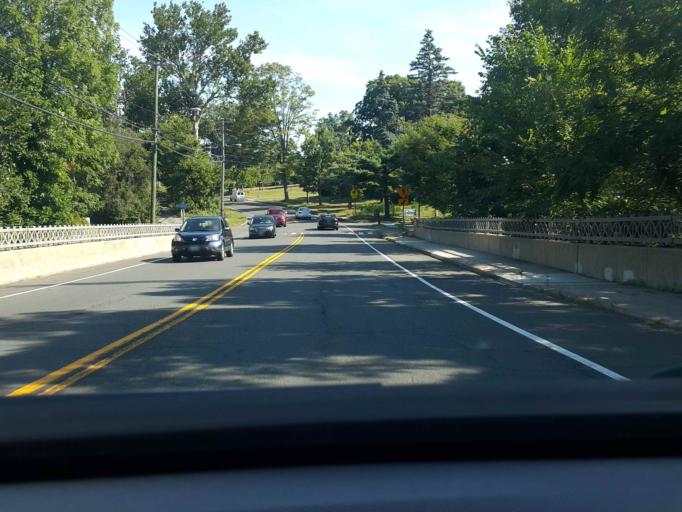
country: US
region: Connecticut
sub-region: Middlesex County
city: Durham
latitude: 41.4737
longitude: -72.6804
